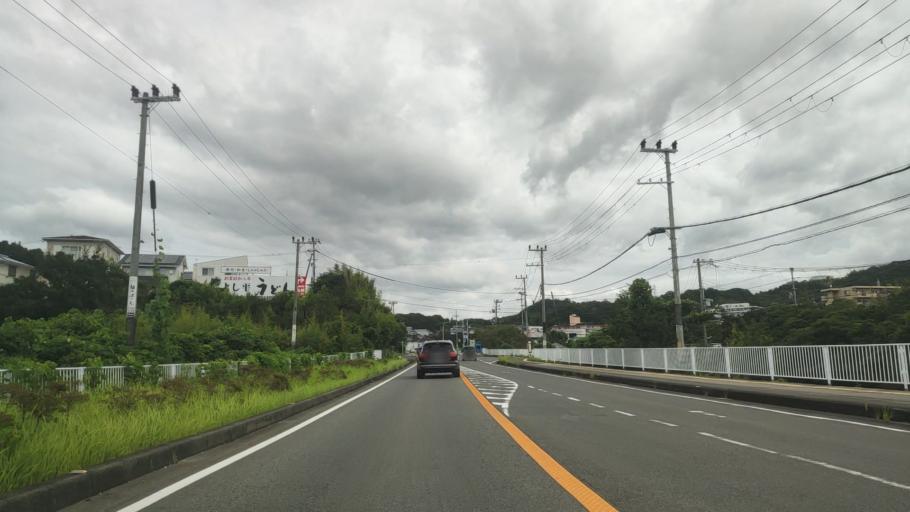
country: JP
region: Wakayama
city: Tanabe
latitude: 33.7050
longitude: 135.3974
